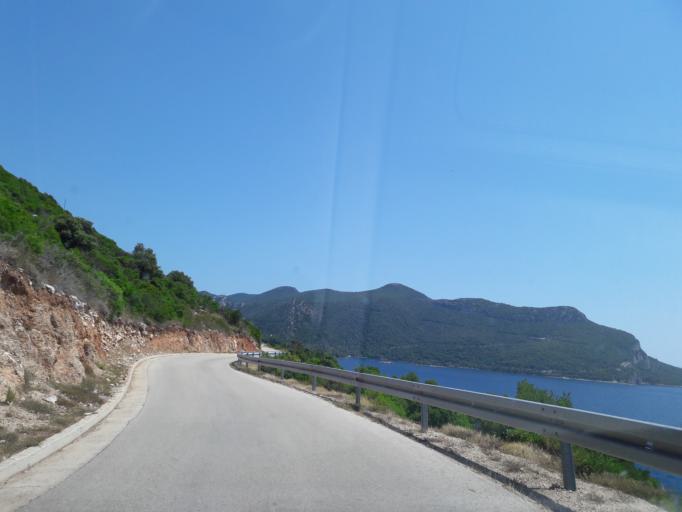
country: HR
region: Dubrovacko-Neretvanska
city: Blato
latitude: 42.9010
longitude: 17.4329
